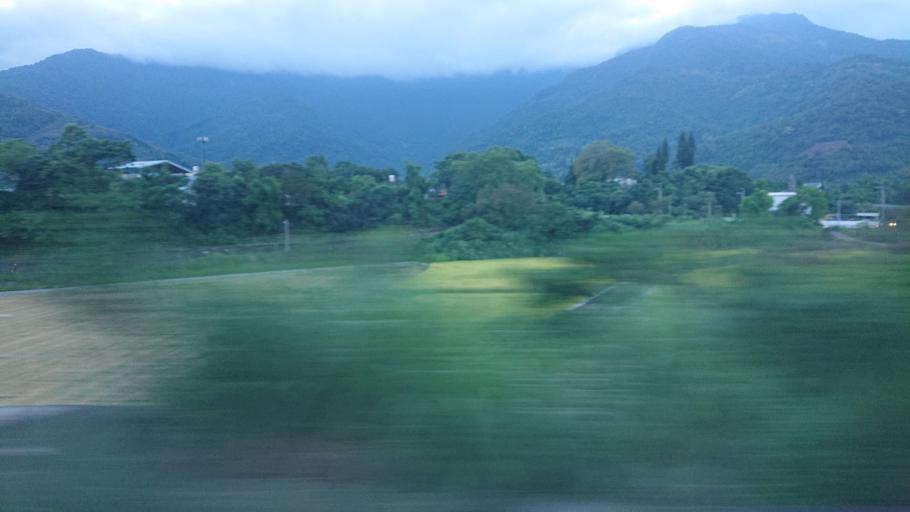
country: TW
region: Taiwan
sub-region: Taitung
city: Taitung
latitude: 23.0399
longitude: 121.1626
